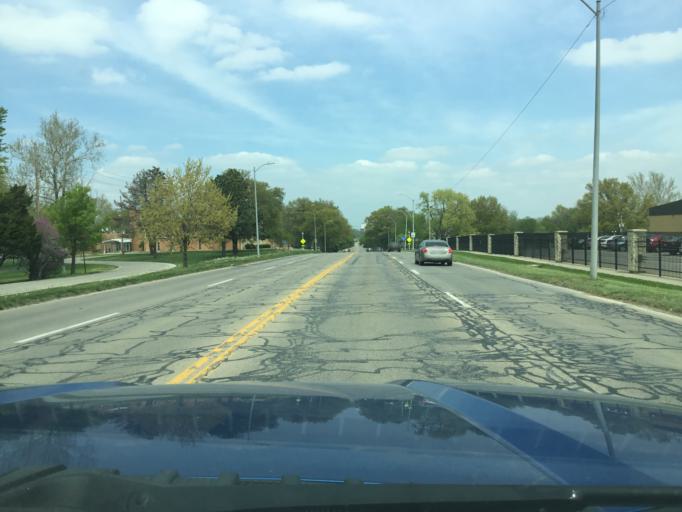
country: US
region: Kansas
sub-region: Shawnee County
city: Topeka
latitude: 39.0211
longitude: -95.6858
